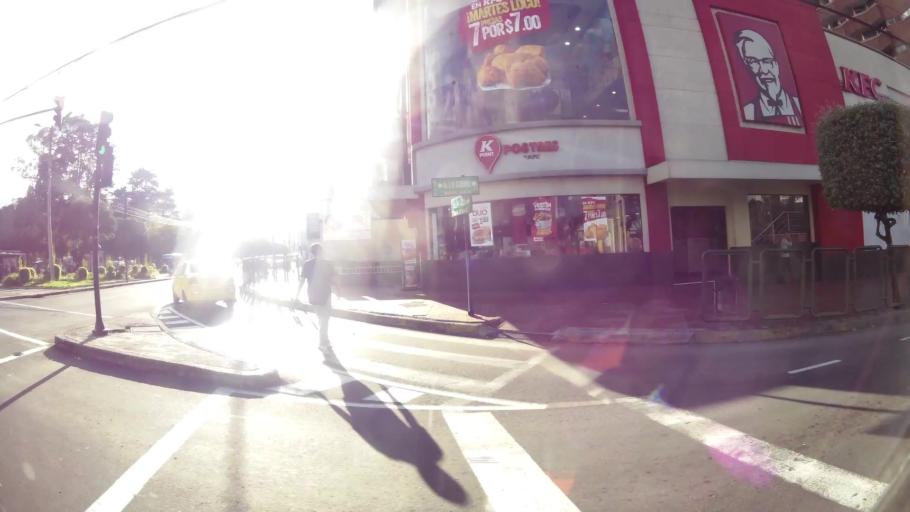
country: EC
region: Pichincha
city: Quito
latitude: -0.2086
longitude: -78.4955
